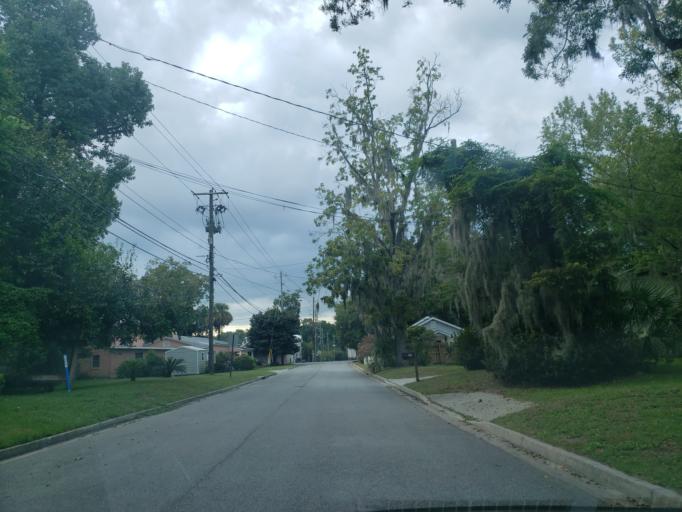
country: US
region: Georgia
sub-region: Chatham County
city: Isle of Hope
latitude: 31.9869
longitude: -81.0716
